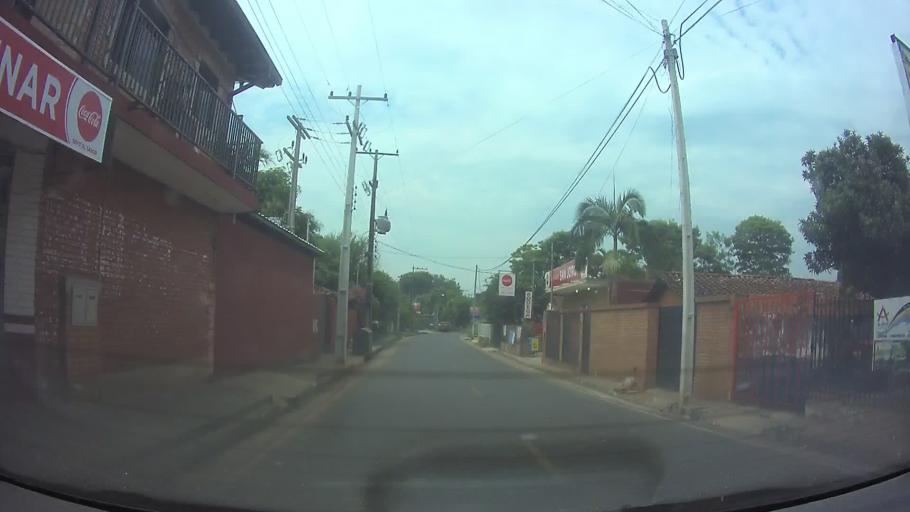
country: PY
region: Central
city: San Lorenzo
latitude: -25.2896
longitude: -57.5045
